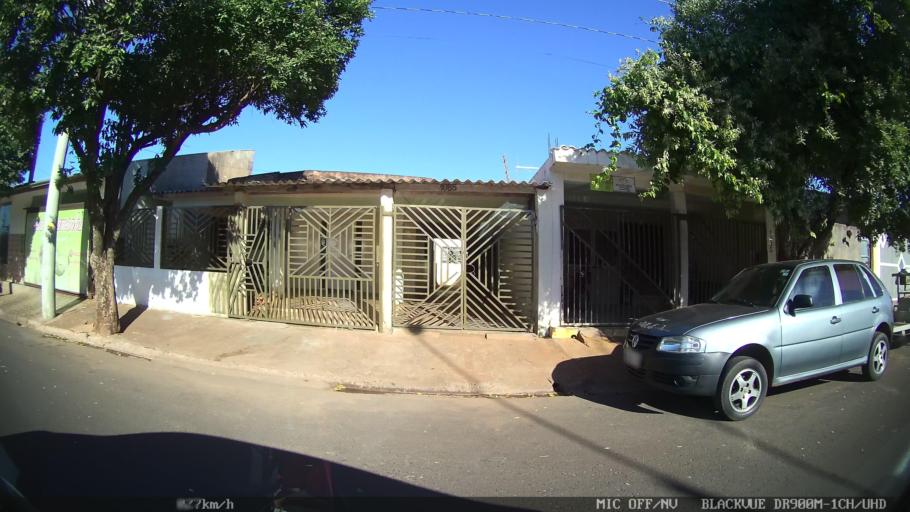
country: BR
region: Sao Paulo
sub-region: Olimpia
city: Olimpia
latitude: -20.7271
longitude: -48.8994
